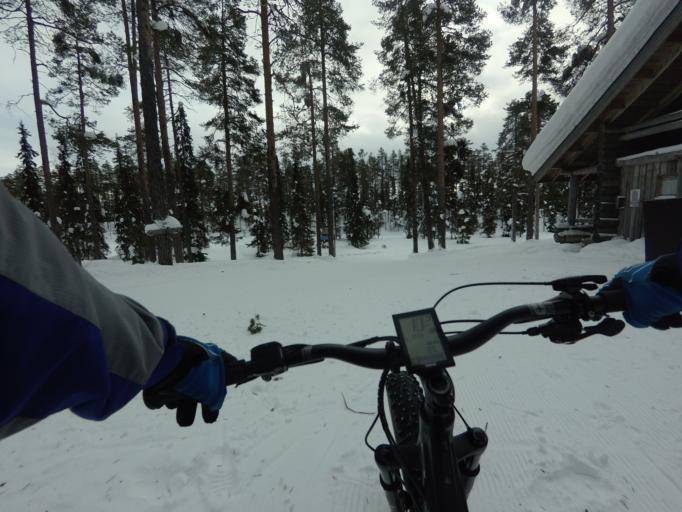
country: FI
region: Lapland
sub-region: Tunturi-Lappi
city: Kolari
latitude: 67.5997
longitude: 24.2994
